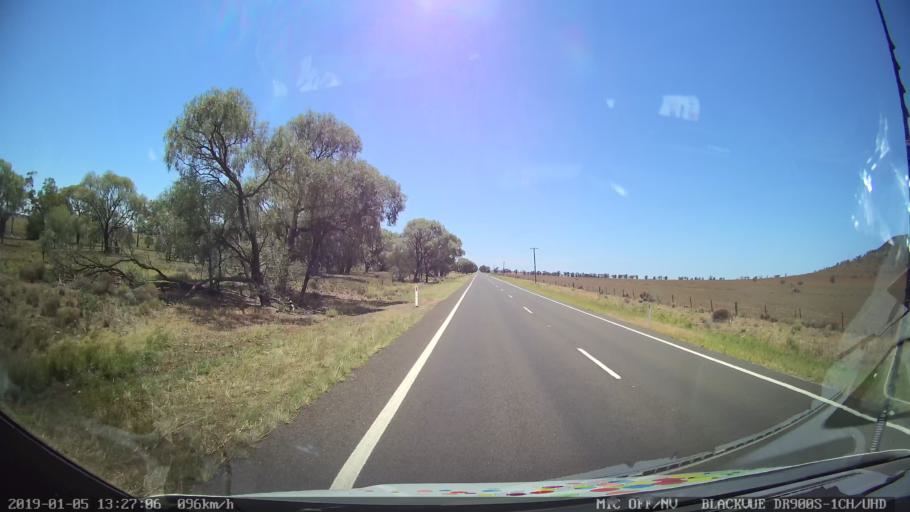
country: AU
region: New South Wales
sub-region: Gunnedah
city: Gunnedah
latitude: -31.0474
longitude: 150.0244
